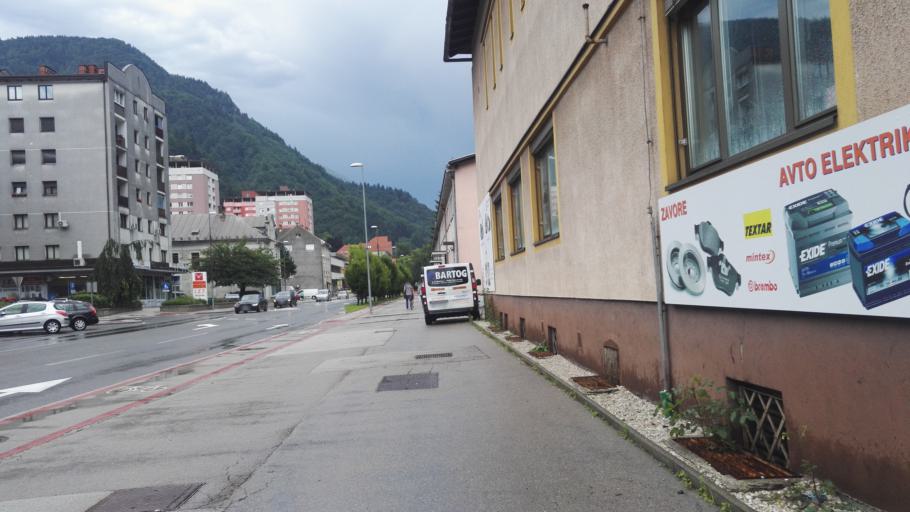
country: SI
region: Jesenice
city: Jesenice
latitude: 46.4364
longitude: 14.0561
